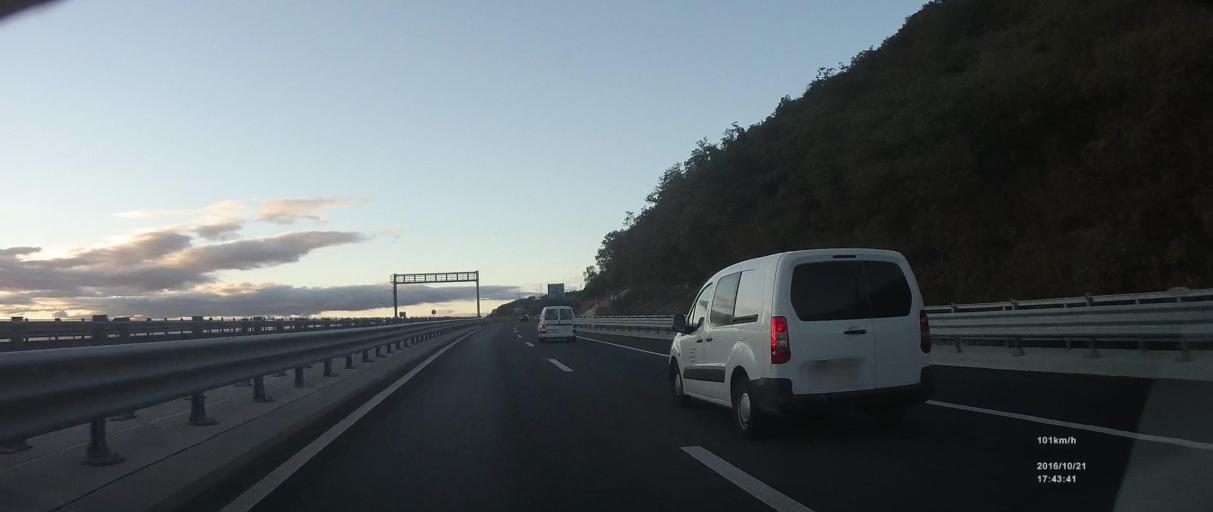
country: HR
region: Primorsko-Goranska
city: Hreljin
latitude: 45.2704
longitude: 14.6032
